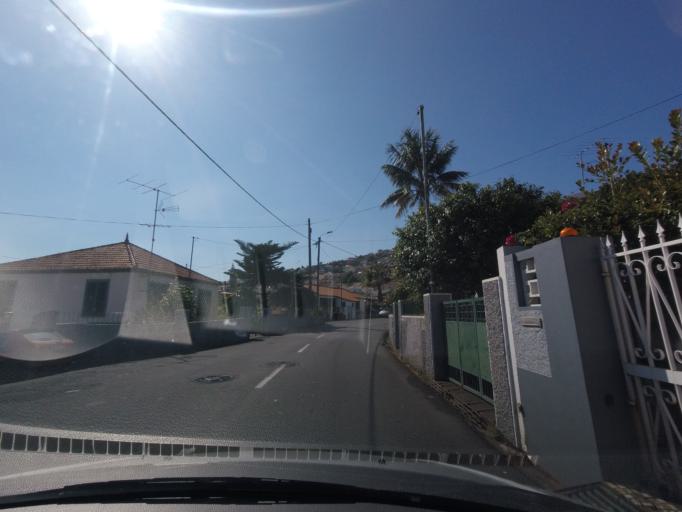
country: PT
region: Madeira
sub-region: Funchal
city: Nossa Senhora do Monte
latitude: 32.6658
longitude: -16.9081
